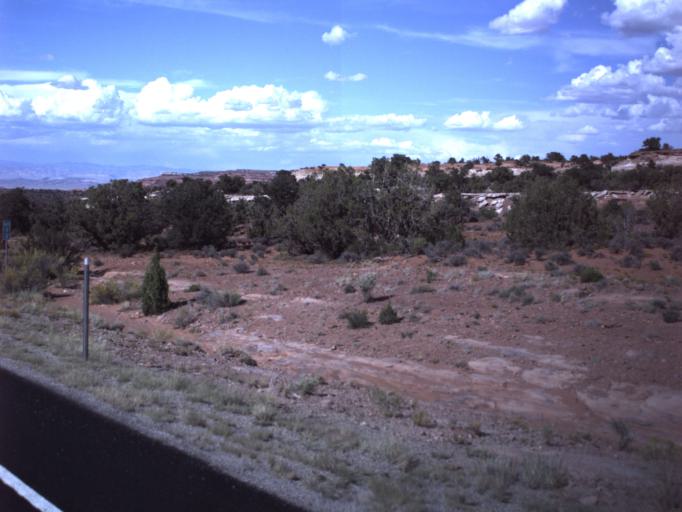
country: US
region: Utah
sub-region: Grand County
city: Moab
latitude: 38.6042
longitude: -109.8172
